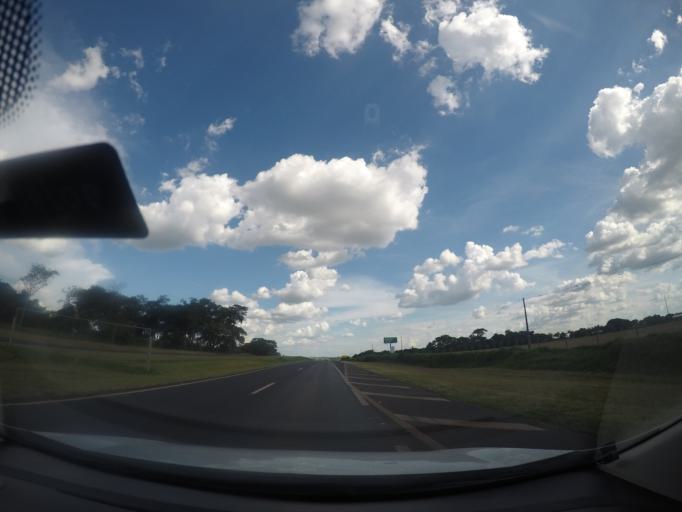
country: BR
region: Sao Paulo
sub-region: Bebedouro
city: Bebedouro
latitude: -20.8842
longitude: -48.4684
